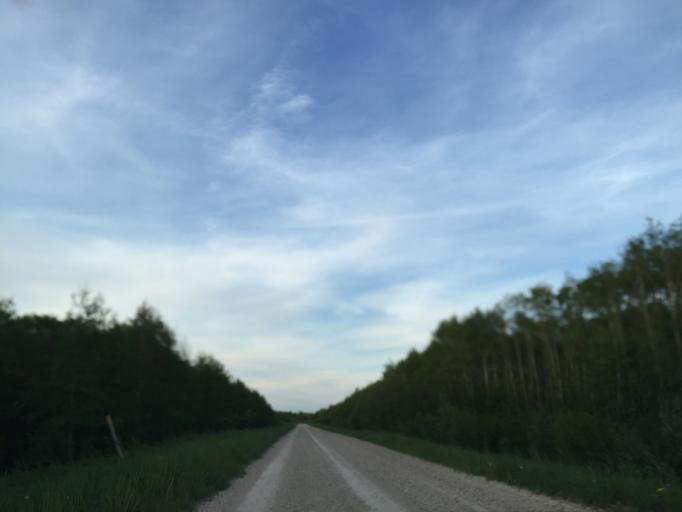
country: LV
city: Tireli
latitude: 56.7478
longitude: 23.5293
